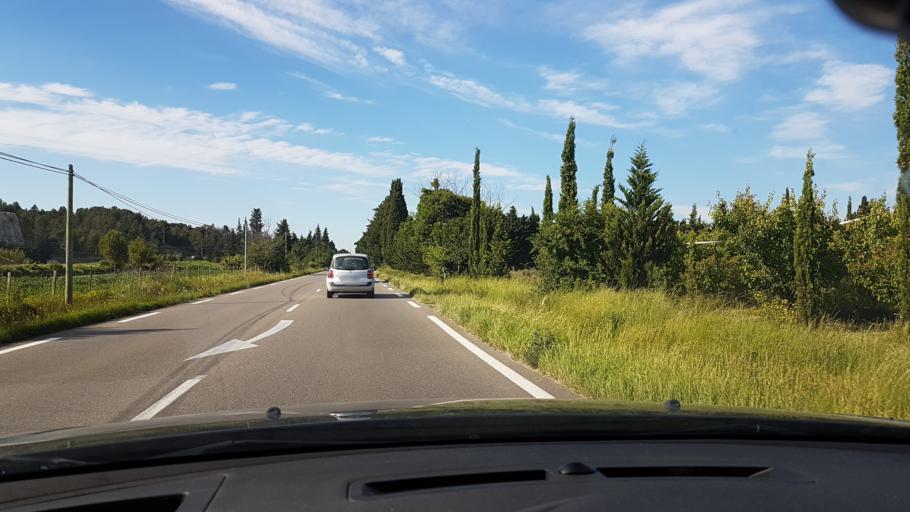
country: FR
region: Provence-Alpes-Cote d'Azur
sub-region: Departement des Bouches-du-Rhone
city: Graveson
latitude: 43.8666
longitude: 4.7701
